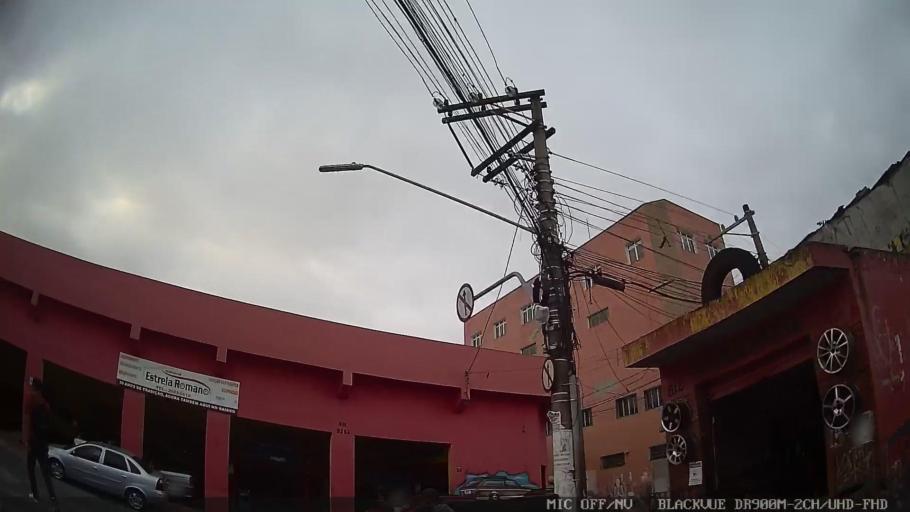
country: BR
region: Sao Paulo
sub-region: Itaquaquecetuba
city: Itaquaquecetuba
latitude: -23.4862
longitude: -46.3896
